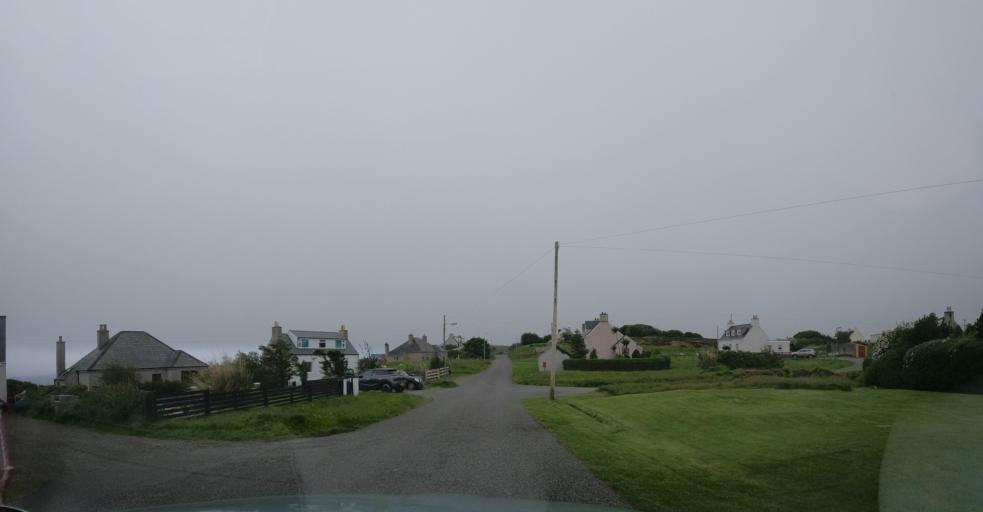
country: GB
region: Scotland
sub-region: Eilean Siar
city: Stornoway
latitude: 58.1976
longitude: -6.2242
